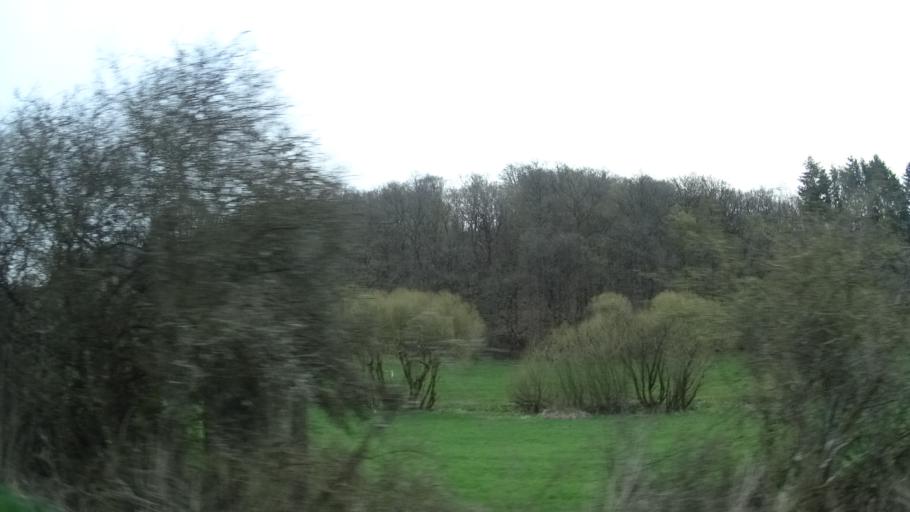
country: DE
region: Rheinland-Pfalz
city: Rimsberg
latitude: 49.6459
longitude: 7.1981
